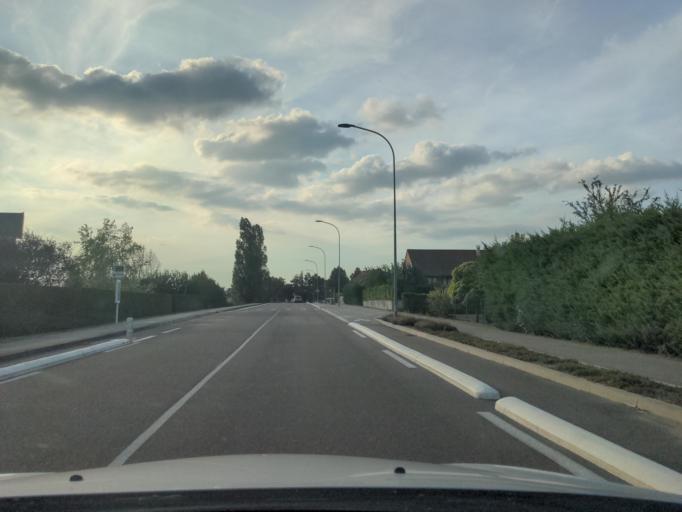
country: FR
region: Bourgogne
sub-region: Departement de la Cote-d'Or
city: Neuilly-les-Dijon
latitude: 47.2785
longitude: 5.1158
